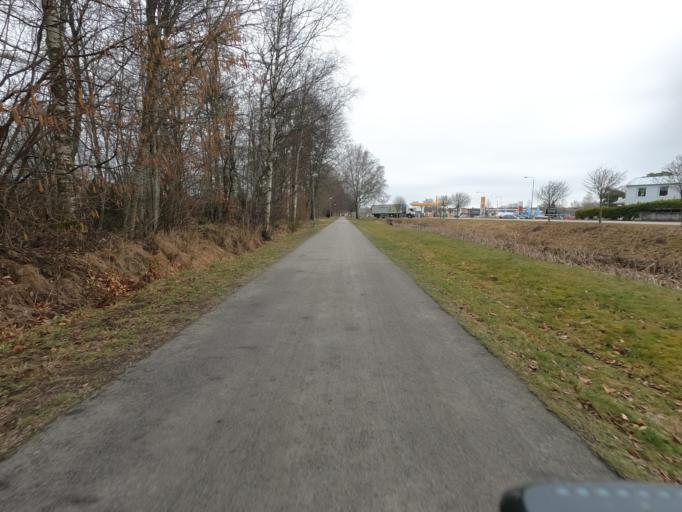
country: SE
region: Kronoberg
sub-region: Ljungby Kommun
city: Ljungby
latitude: 56.8300
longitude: 13.9202
